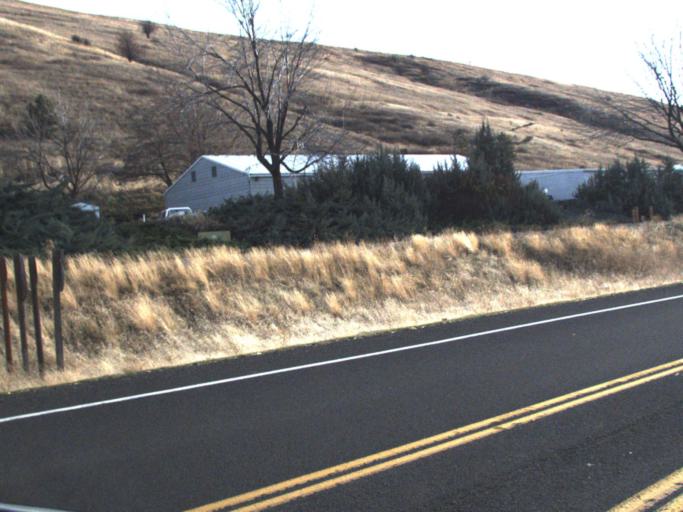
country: US
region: Washington
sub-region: Columbia County
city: Dayton
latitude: 46.3122
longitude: -117.9921
